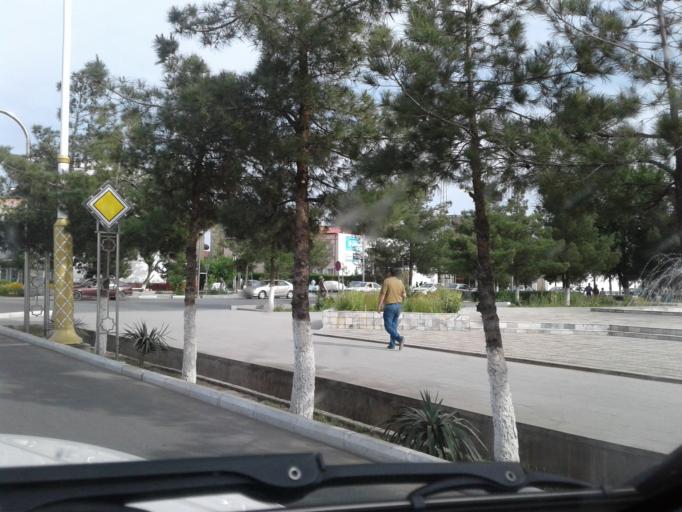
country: TM
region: Mary
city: Mary
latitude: 37.5933
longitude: 61.8409
